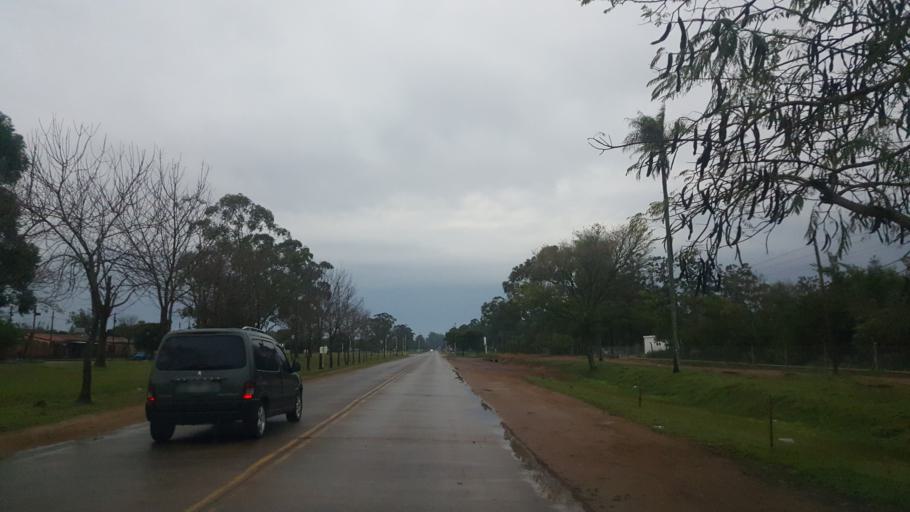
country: AR
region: Corrientes
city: Ituzaingo
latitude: -27.5899
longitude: -56.6847
